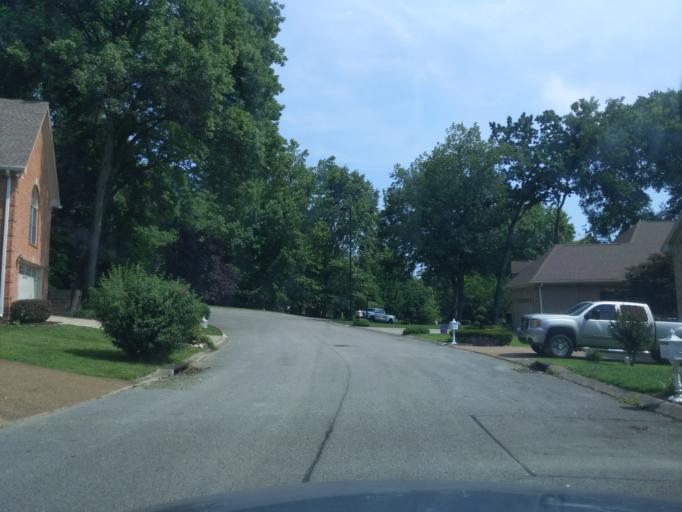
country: US
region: Tennessee
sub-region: Williamson County
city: Brentwood Estates
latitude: 36.0364
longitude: -86.7490
